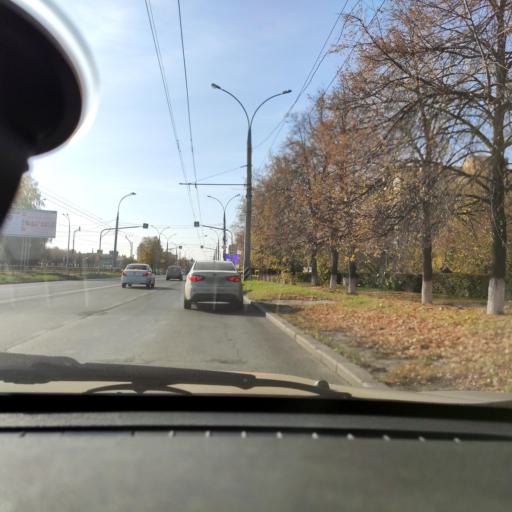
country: RU
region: Samara
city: Tol'yatti
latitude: 53.5165
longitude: 49.2730
